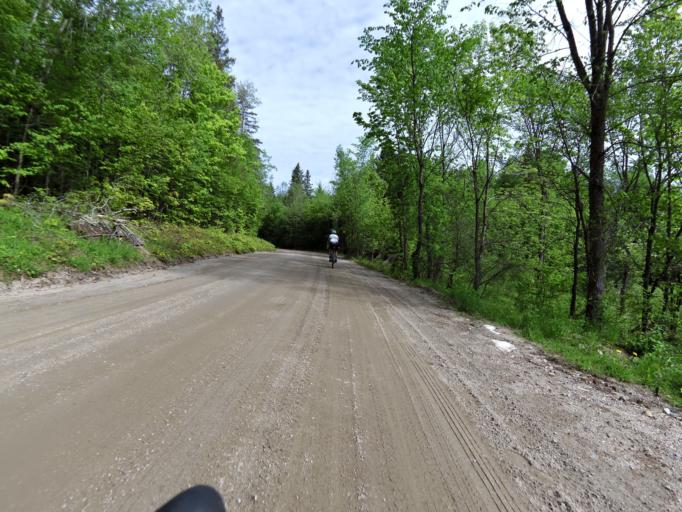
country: CA
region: Quebec
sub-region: Outaouais
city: Wakefield
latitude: 45.7087
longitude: -75.8915
